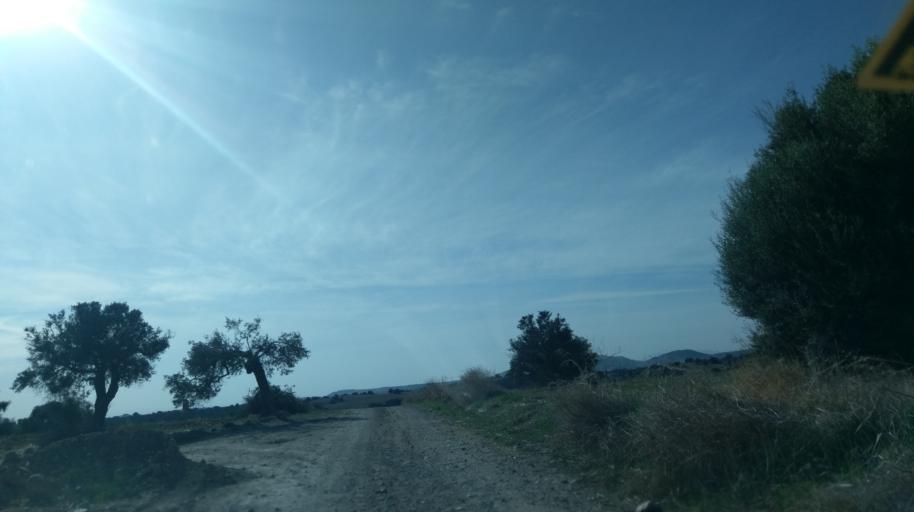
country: CY
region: Ammochostos
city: Trikomo
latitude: 35.3403
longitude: 33.8574
